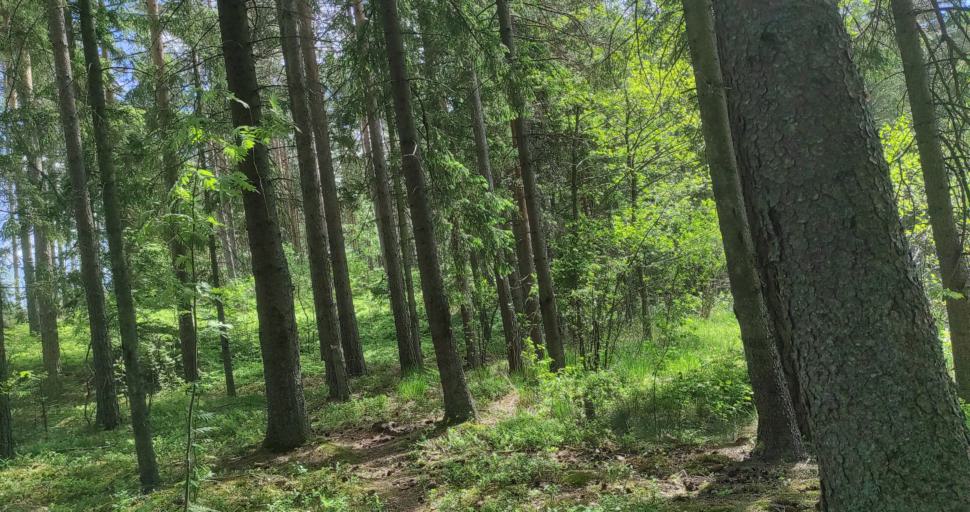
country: LV
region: Talsu Rajons
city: Stende
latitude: 57.1278
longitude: 22.2847
